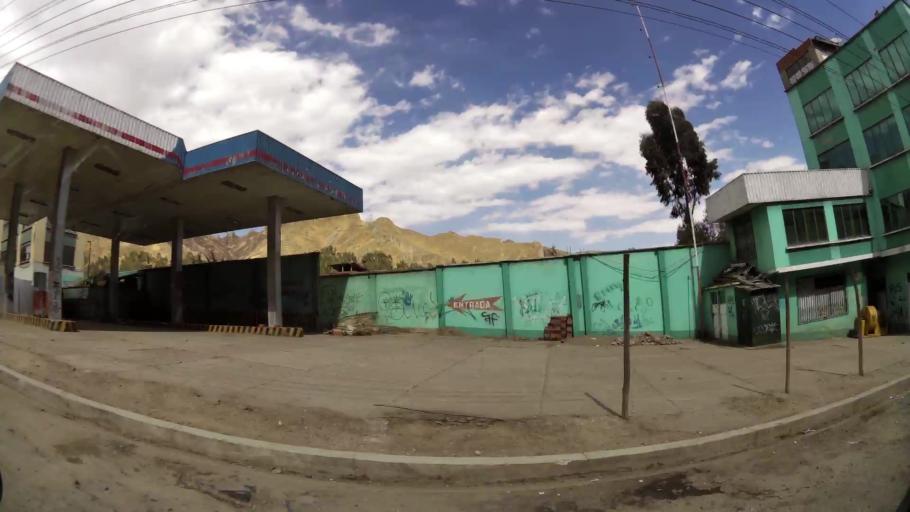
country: BO
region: La Paz
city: La Paz
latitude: -16.4645
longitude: -68.1095
